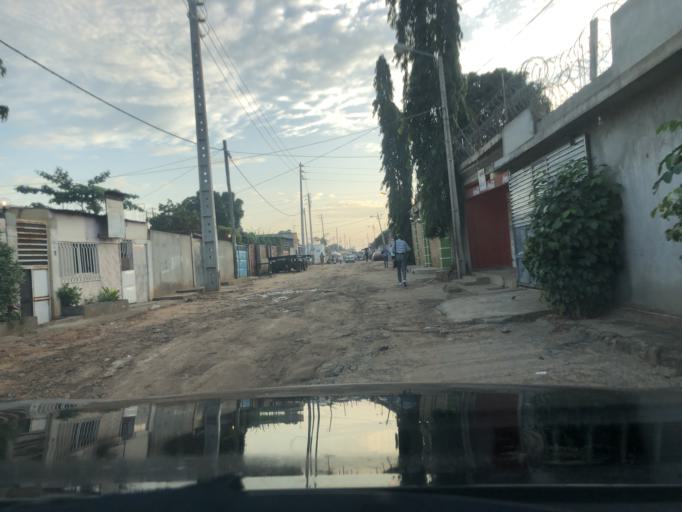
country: AO
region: Luanda
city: Luanda
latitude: -8.8727
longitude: 13.2099
